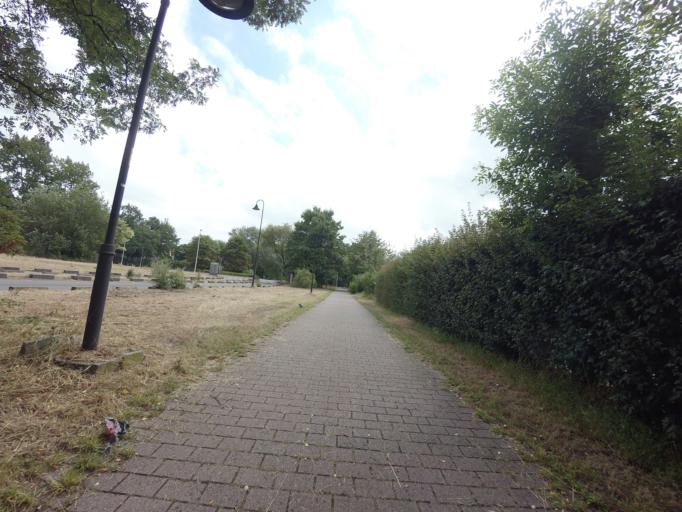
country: BE
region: Flanders
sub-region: Provincie Antwerpen
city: Edegem
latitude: 51.1780
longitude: 4.4169
